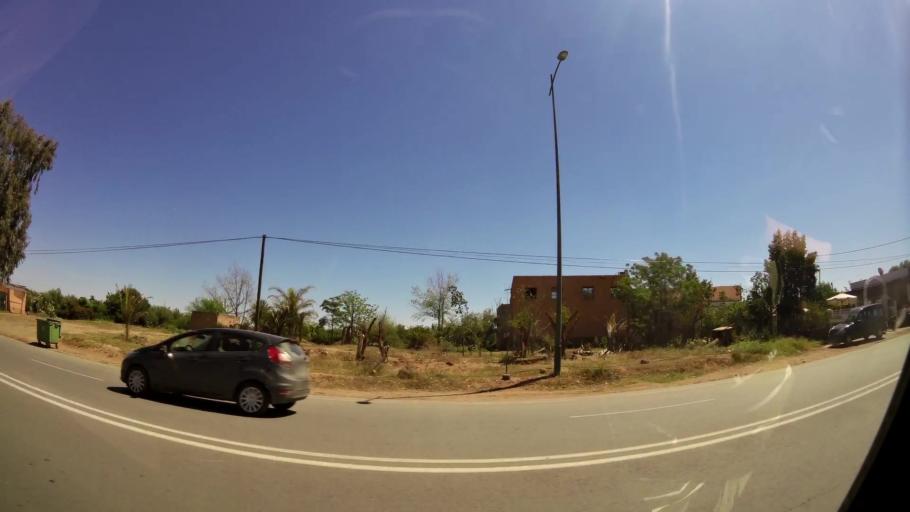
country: MA
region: Marrakech-Tensift-Al Haouz
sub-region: Marrakech
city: Marrakesh
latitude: 31.5621
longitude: -7.9787
